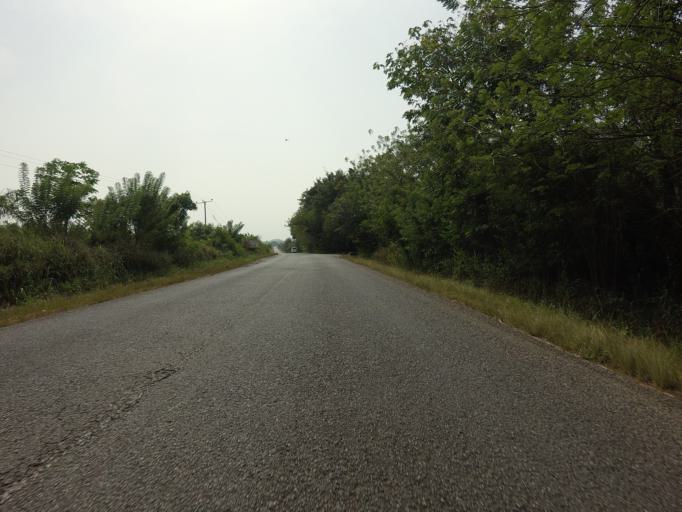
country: GH
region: Volta
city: Ho
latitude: 6.3975
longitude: 0.1789
